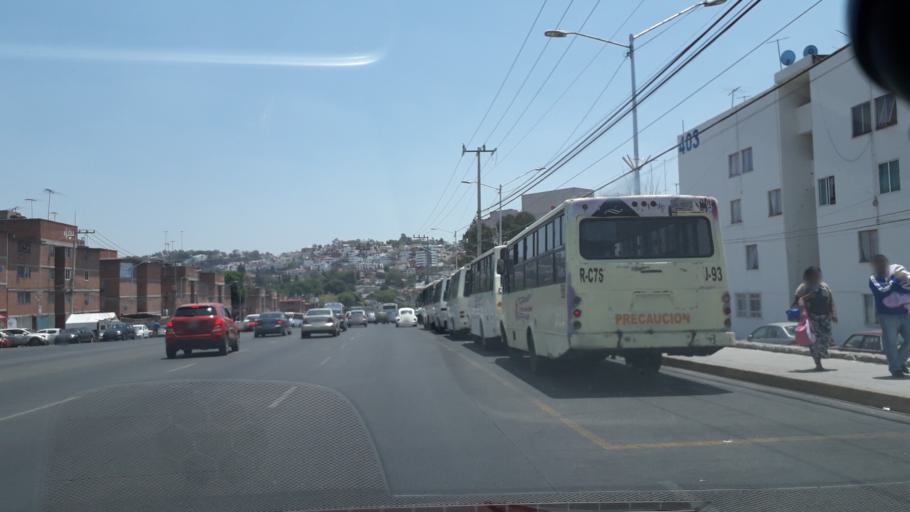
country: MX
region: Puebla
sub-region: Puebla
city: Galaxia la Calera
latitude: 19.0095
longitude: -98.1847
